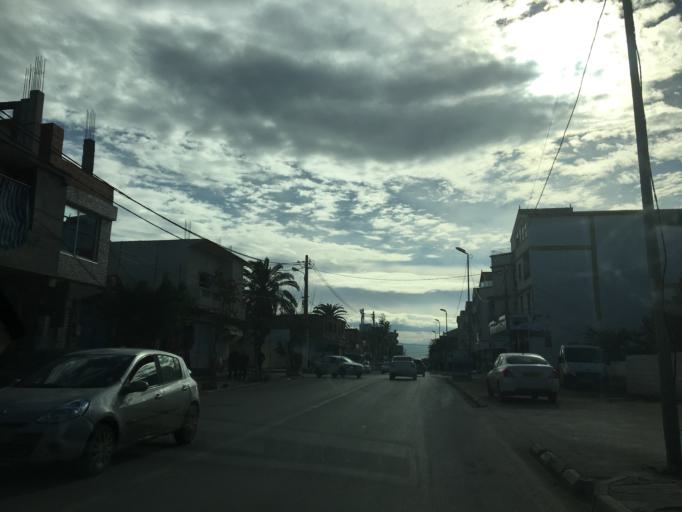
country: DZ
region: Alger
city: Ain Taya
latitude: 36.7822
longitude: 3.2490
